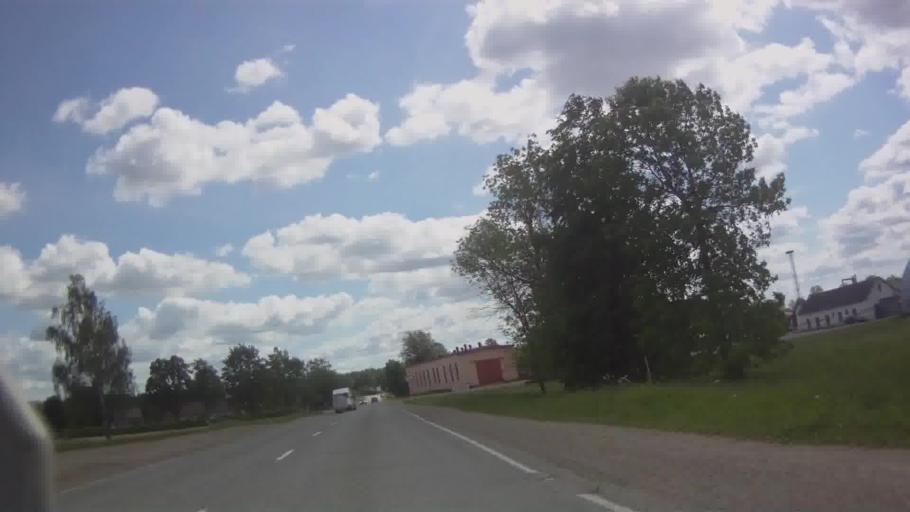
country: LV
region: Vilanu
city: Vilani
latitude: 56.5694
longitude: 26.9244
